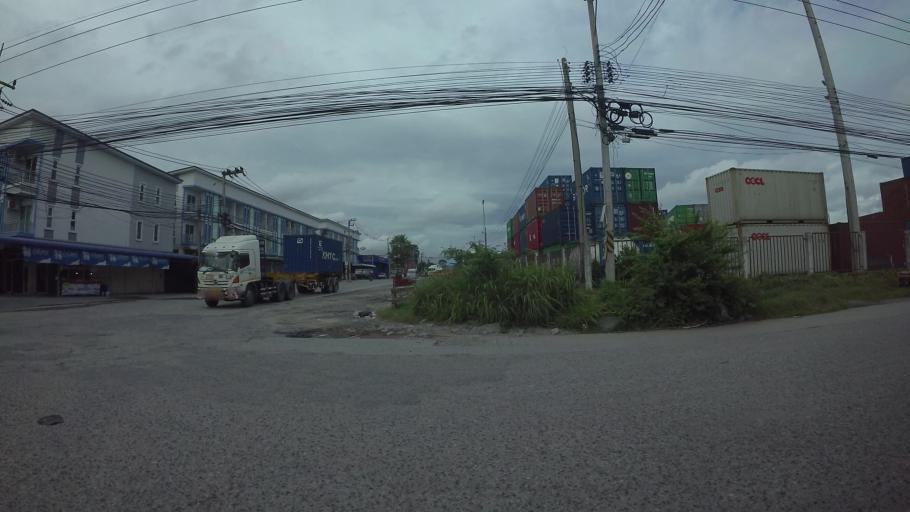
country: TH
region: Chon Buri
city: Ban Talat Bueng
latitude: 13.1219
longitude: 100.9725
